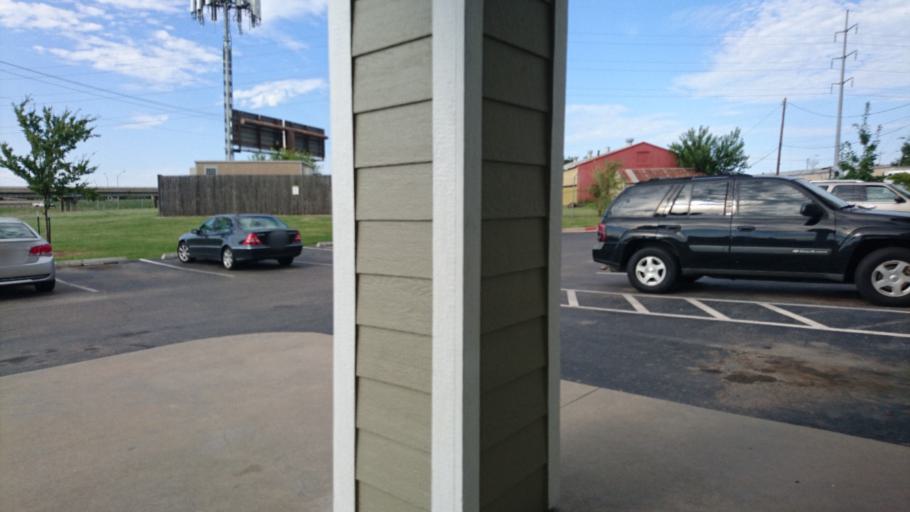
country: US
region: Oklahoma
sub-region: Oklahoma County
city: Warr Acres
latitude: 35.5093
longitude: -97.5744
